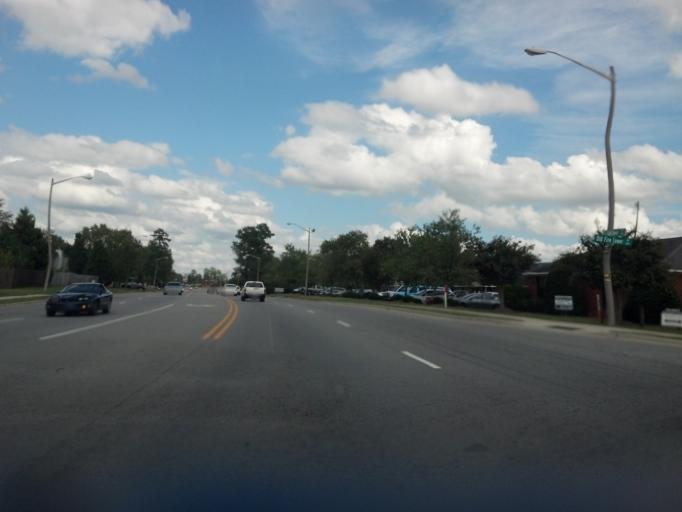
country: US
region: North Carolina
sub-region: Pitt County
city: Windsor
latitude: 35.5599
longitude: -77.3646
